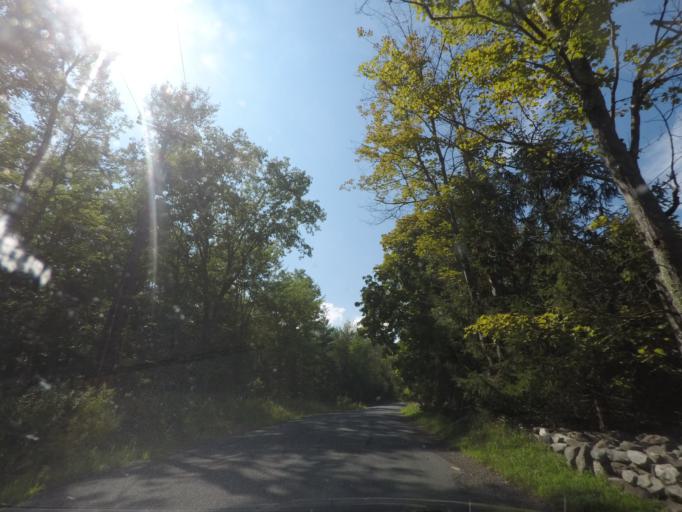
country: US
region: New York
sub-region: Rensselaer County
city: Averill Park
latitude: 42.5913
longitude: -73.5746
